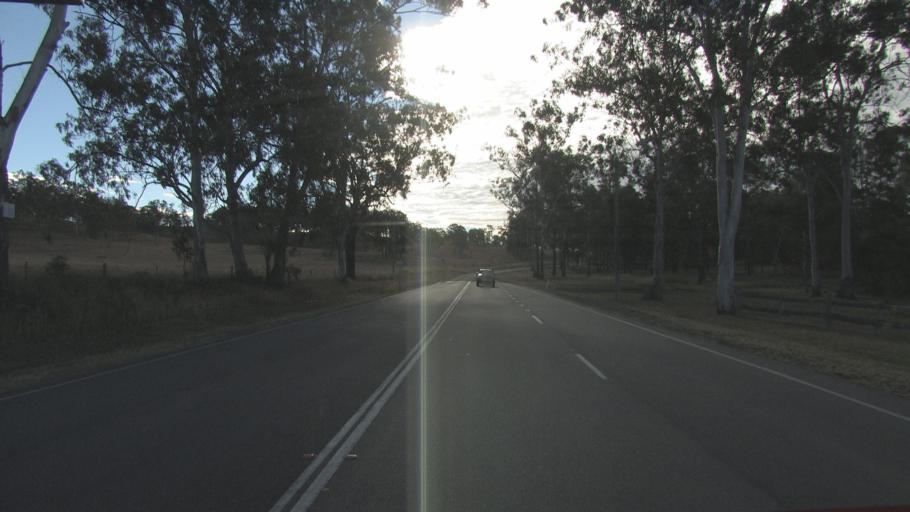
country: AU
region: Queensland
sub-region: Logan
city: Cedar Vale
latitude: -27.8769
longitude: 153.0677
